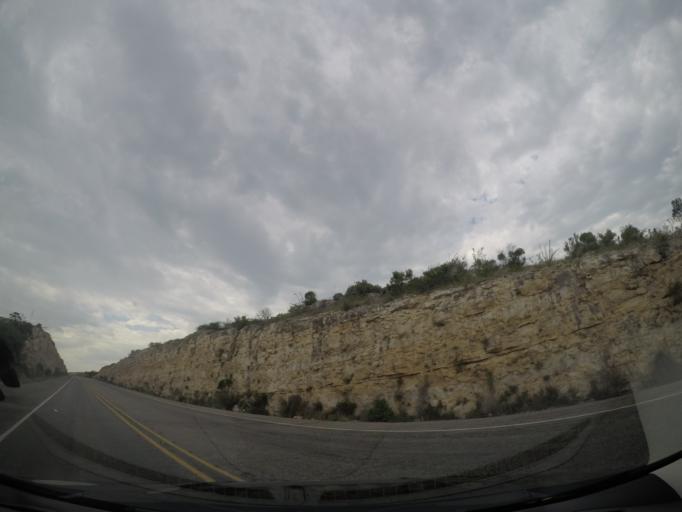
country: US
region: Texas
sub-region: Val Verde County
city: Cienegas Terrace
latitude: 29.7074
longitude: -101.3502
